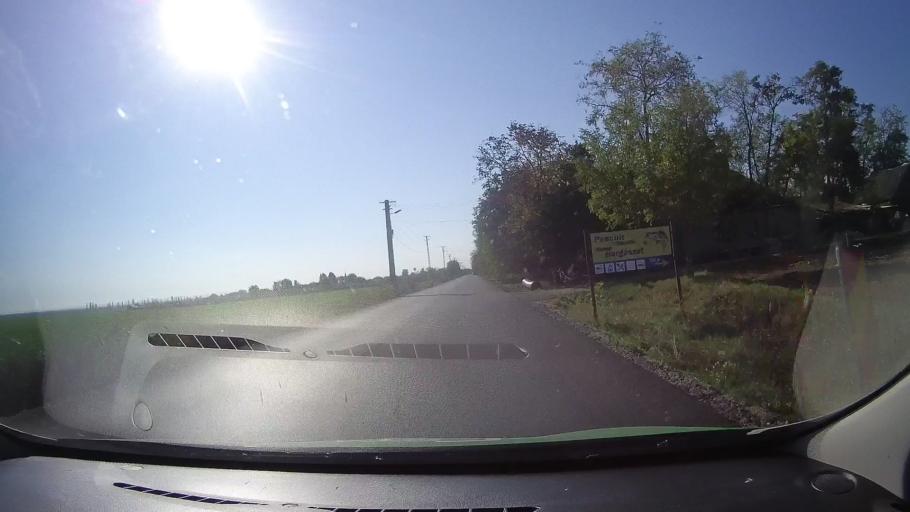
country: RO
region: Satu Mare
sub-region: Comuna Tiream
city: Tiream
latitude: 47.6226
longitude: 22.4680
